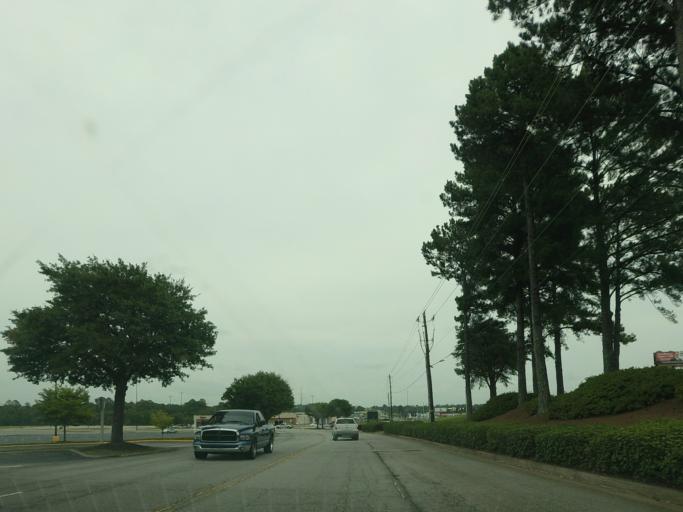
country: US
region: Georgia
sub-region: Bibb County
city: Macon
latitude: 32.8161
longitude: -83.6931
